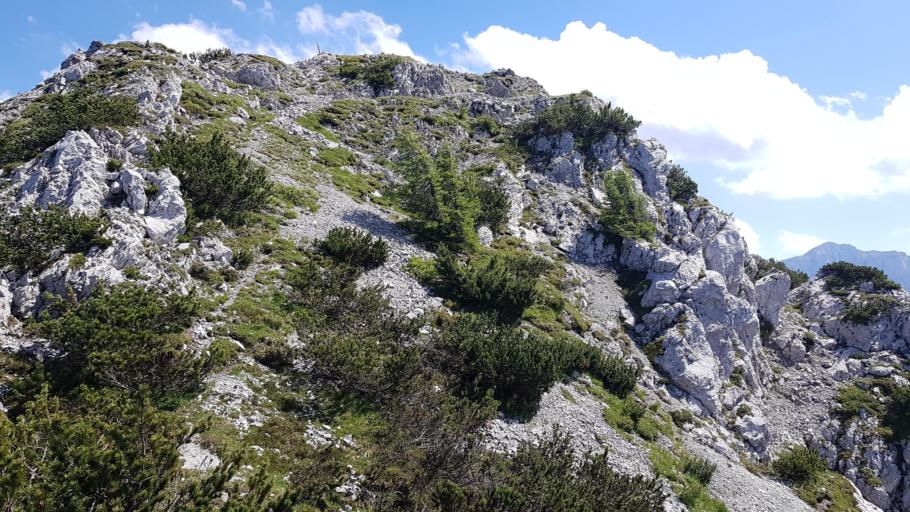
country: IT
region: Friuli Venezia Giulia
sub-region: Provincia di Udine
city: Malborghetto
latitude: 46.4750
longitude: 13.3976
